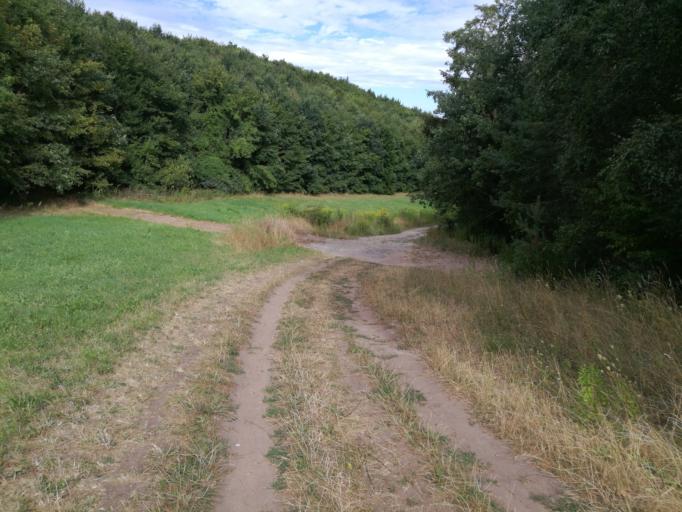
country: DE
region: Bavaria
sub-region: Regierungsbezirk Mittelfranken
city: Seukendorf
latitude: 49.4755
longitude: 10.9106
